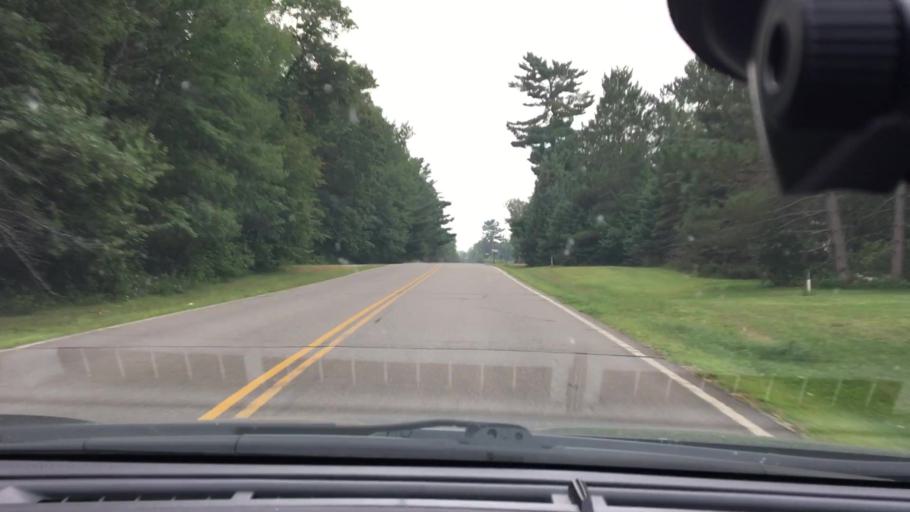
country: US
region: Minnesota
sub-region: Crow Wing County
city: Cross Lake
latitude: 46.6423
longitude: -94.0097
